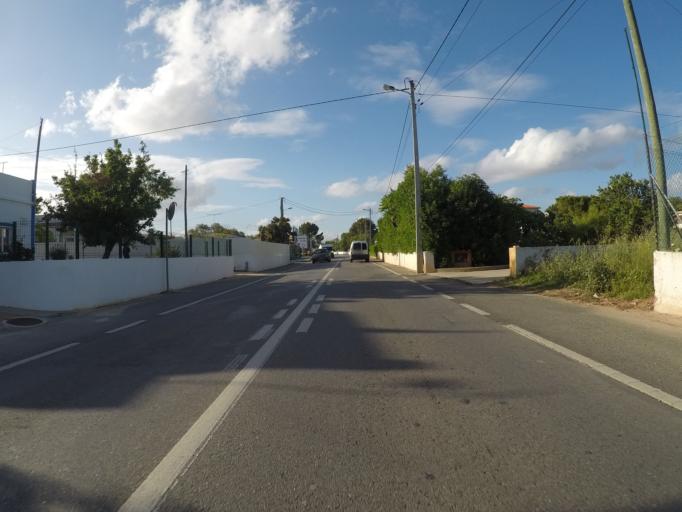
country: PT
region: Faro
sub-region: Lagoa
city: Lagoa
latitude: 37.1144
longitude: -8.4551
